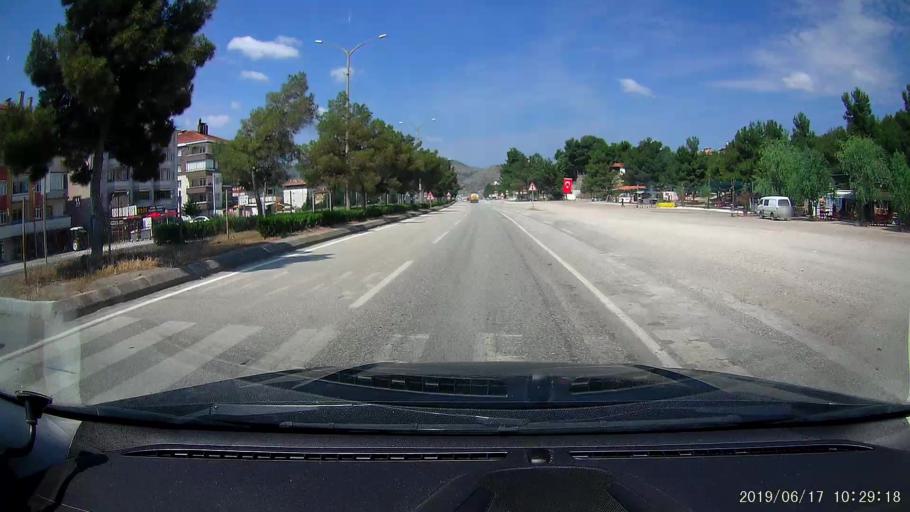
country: TR
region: Corum
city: Osmancik
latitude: 40.9798
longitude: 34.7959
